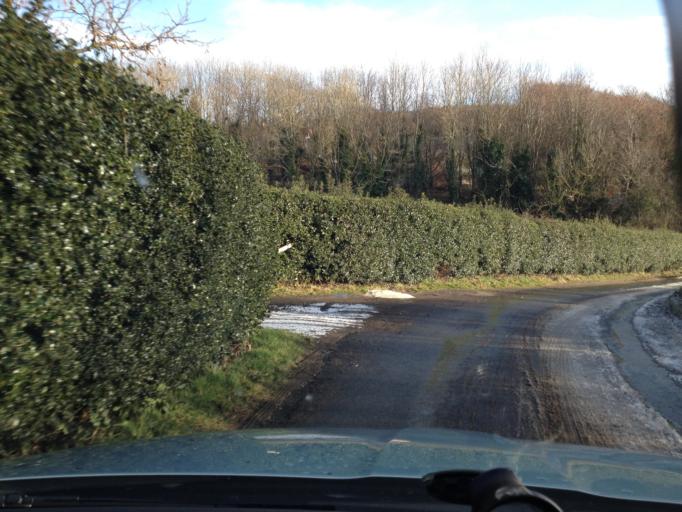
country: GB
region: Scotland
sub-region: Perth and Kinross
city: Bridge of Earn
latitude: 56.3659
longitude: -3.4298
